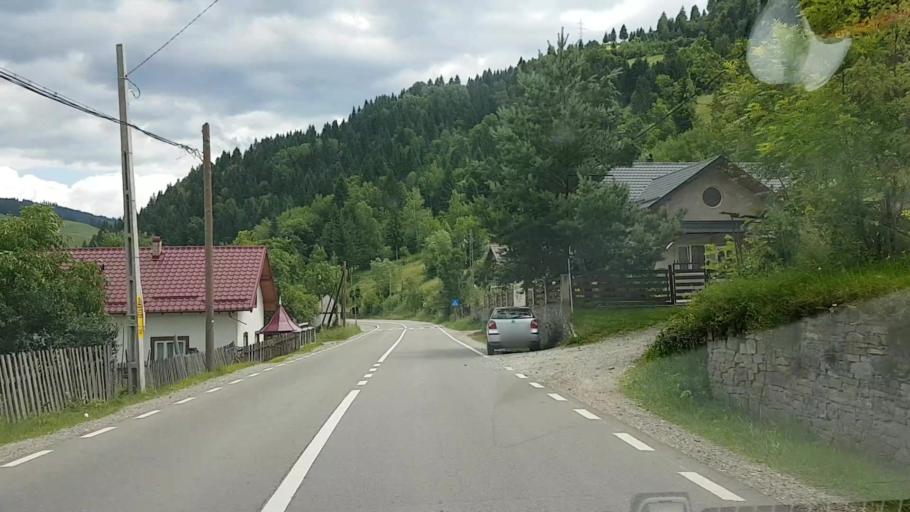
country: RO
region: Neamt
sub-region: Comuna Farcasa
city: Farcasa
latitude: 47.1357
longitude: 25.8736
